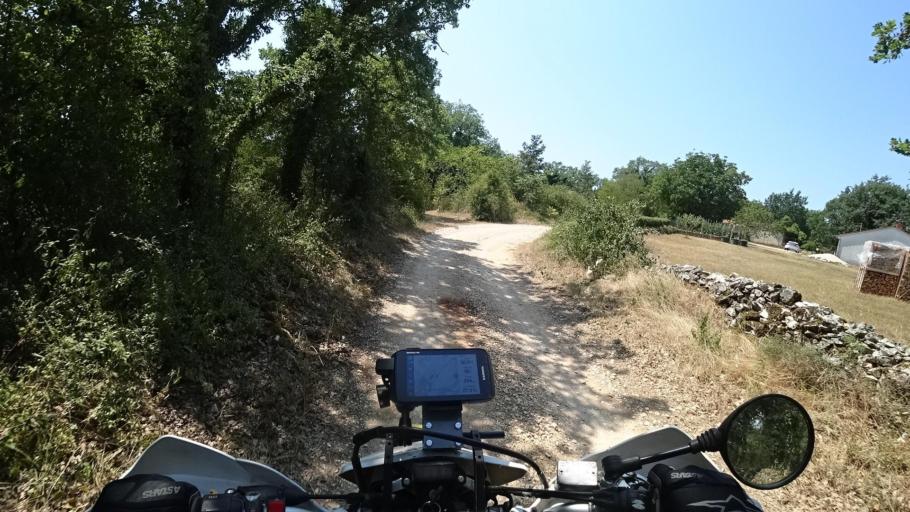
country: HR
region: Istarska
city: Karojba
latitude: 45.2617
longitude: 13.7784
